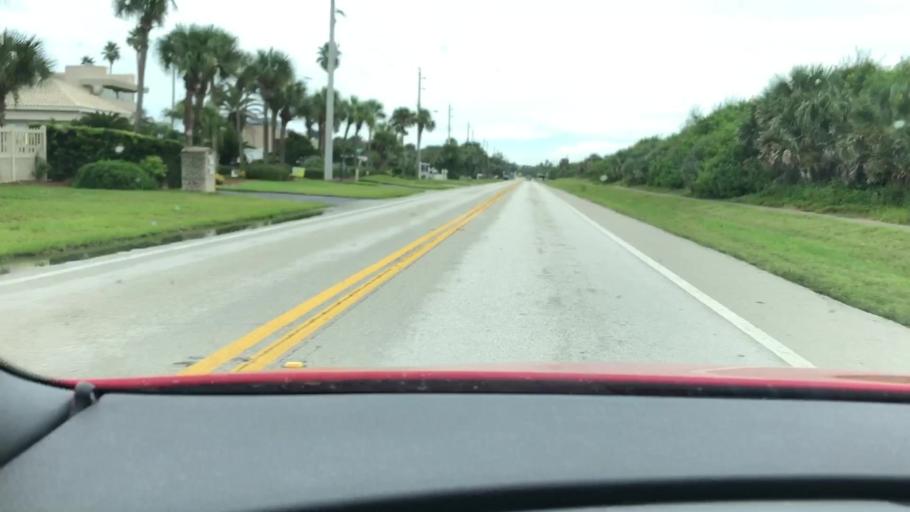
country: US
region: Florida
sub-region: Volusia County
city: Ormond Beach
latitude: 29.3049
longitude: -81.0464
